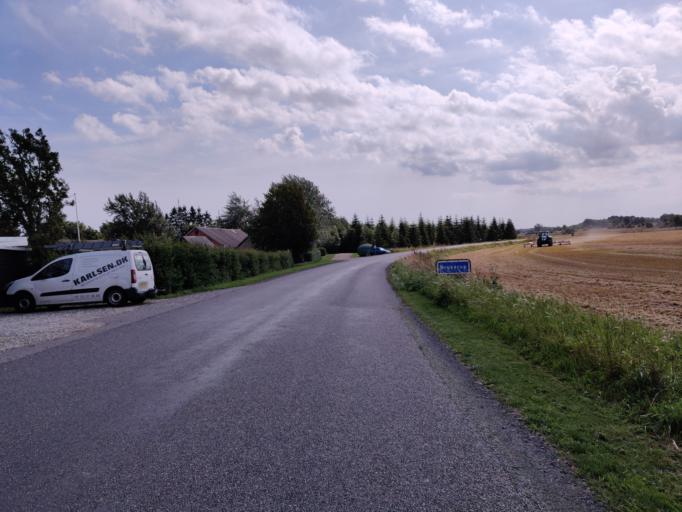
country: DK
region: Zealand
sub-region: Guldborgsund Kommune
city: Nykobing Falster
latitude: 54.6738
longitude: 11.9006
